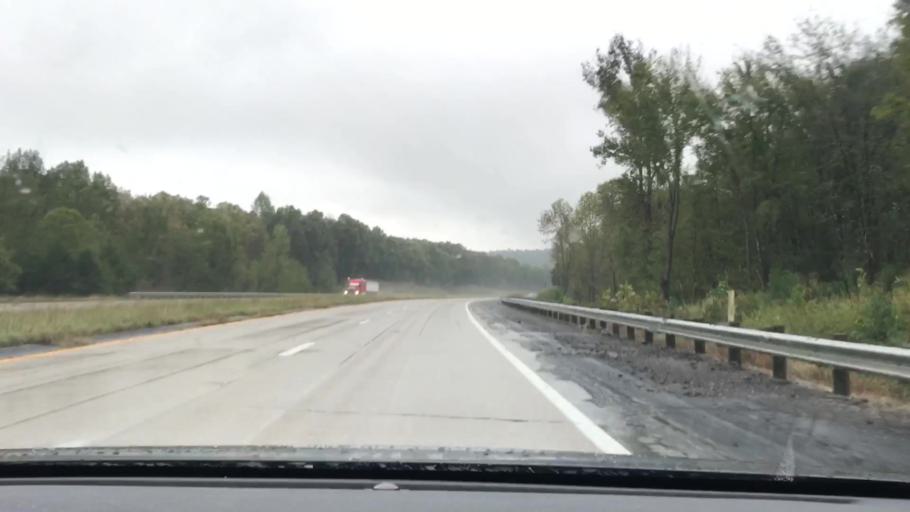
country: US
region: Kentucky
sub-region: Hopkins County
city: Nortonville
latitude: 37.1345
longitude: -87.4584
